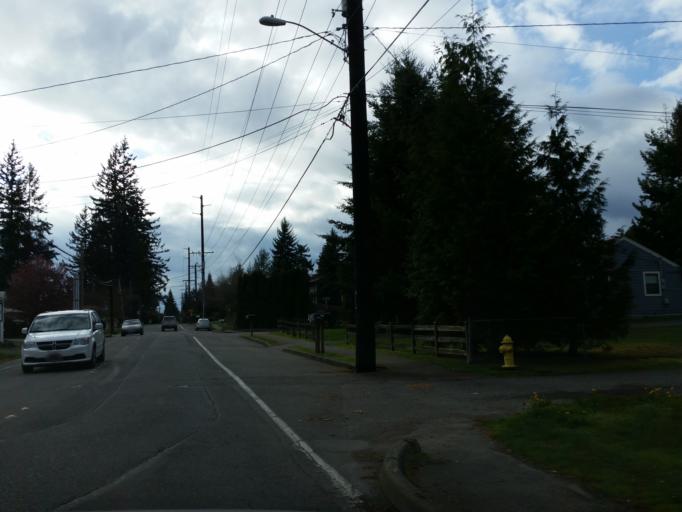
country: US
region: Washington
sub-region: Snohomish County
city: Lynnwood
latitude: 47.8285
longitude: -122.3167
